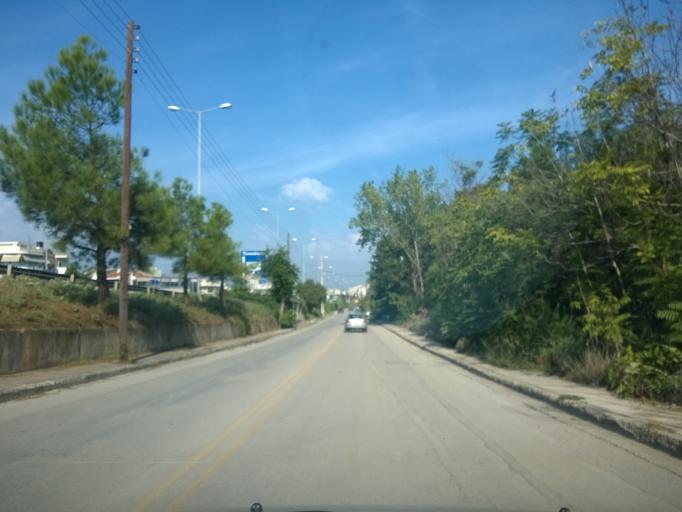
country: GR
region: Central Macedonia
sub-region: Nomos Thessalonikis
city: Pylaia
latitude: 40.5885
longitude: 22.9696
